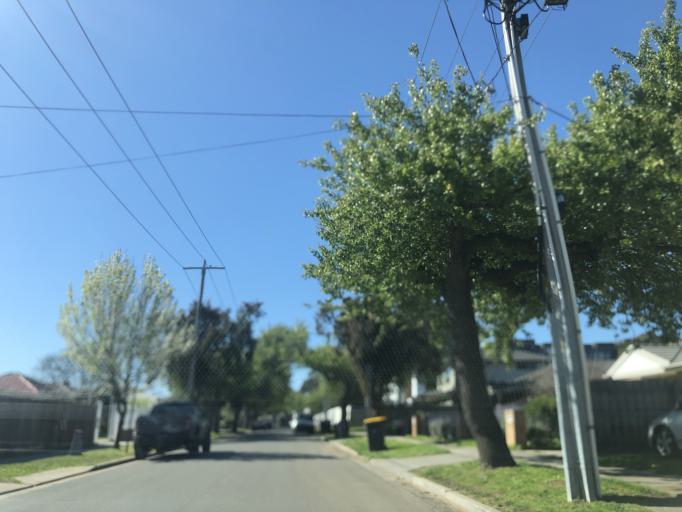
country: AU
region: Victoria
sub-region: Monash
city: Clayton
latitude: -37.9189
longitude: 145.1421
